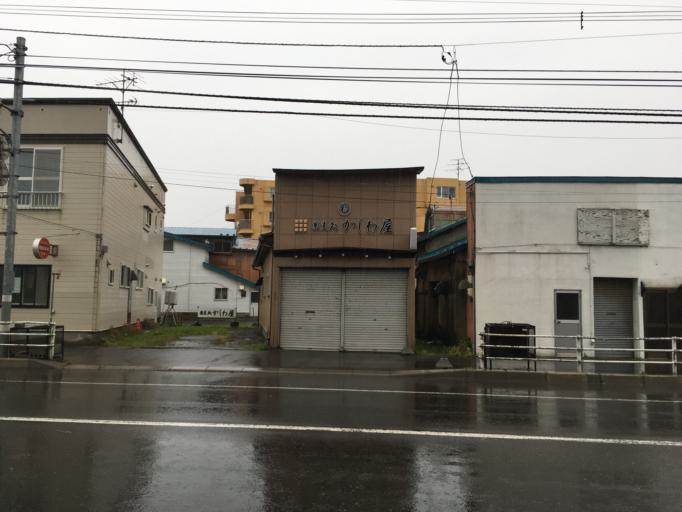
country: JP
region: Hokkaido
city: Hakodate
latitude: 41.7748
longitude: 140.7319
